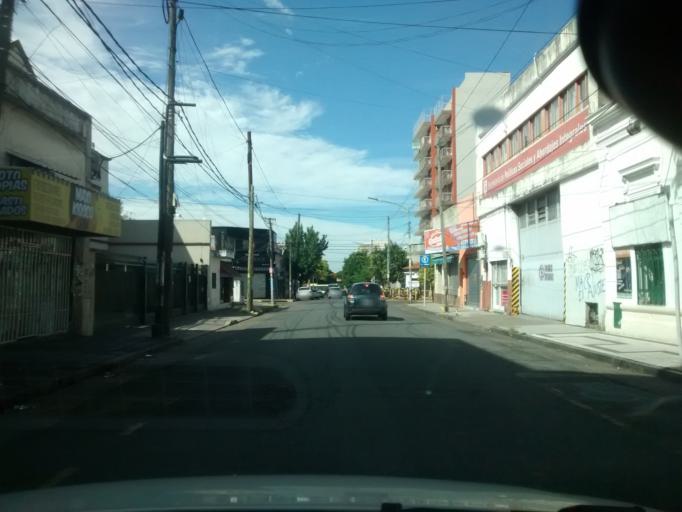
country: AR
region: Buenos Aires
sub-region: Partido de Moron
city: Moron
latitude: -34.6533
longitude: -58.6227
